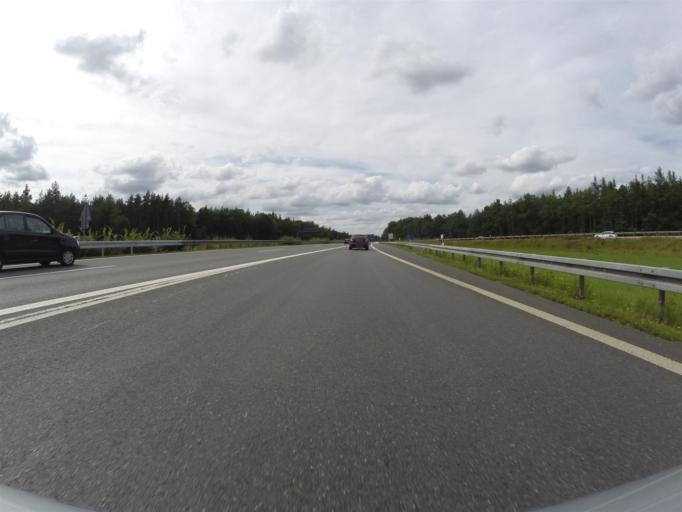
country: DE
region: Bavaria
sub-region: Regierungsbezirk Mittelfranken
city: Wendelstein
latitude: 49.3799
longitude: 11.1334
